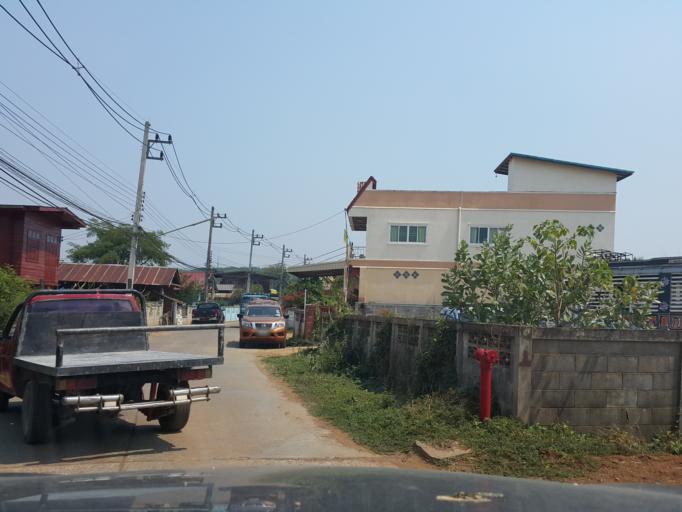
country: TH
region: Sukhothai
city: Thung Saliam
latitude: 17.3142
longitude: 99.5532
